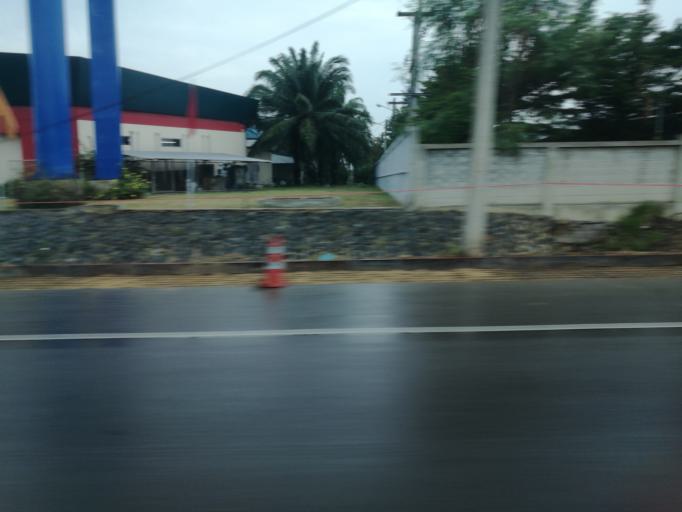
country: TH
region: Prachuap Khiri Khan
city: Kui Buri
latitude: 12.1033
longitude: 99.8534
